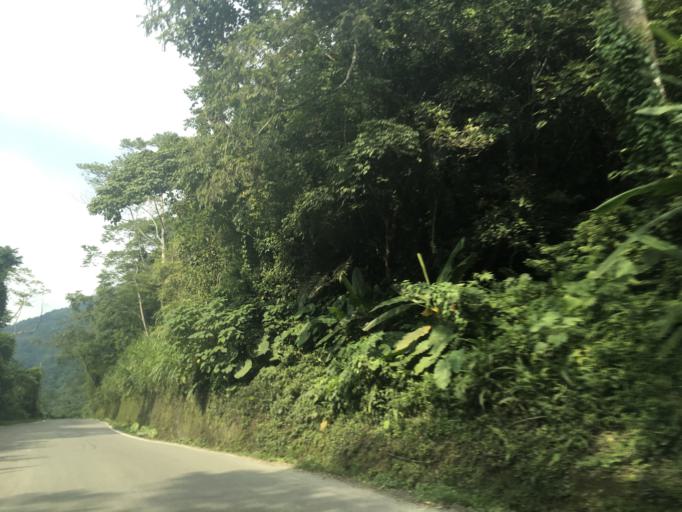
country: TW
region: Taiwan
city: Fengyuan
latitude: 24.3425
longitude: 120.9407
